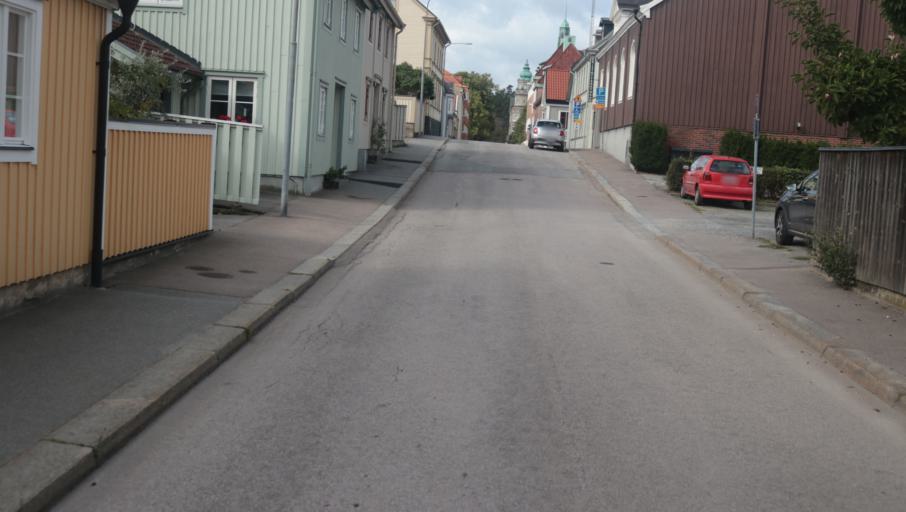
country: SE
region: Blekinge
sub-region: Karlshamns Kommun
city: Karlshamn
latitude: 56.1716
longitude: 14.8665
